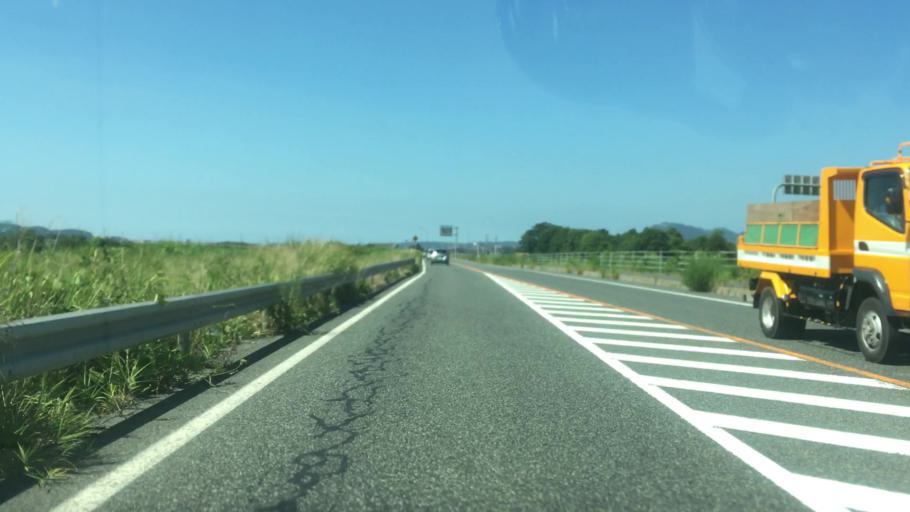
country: JP
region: Tottori
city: Tottori
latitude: 35.4531
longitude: 134.2149
